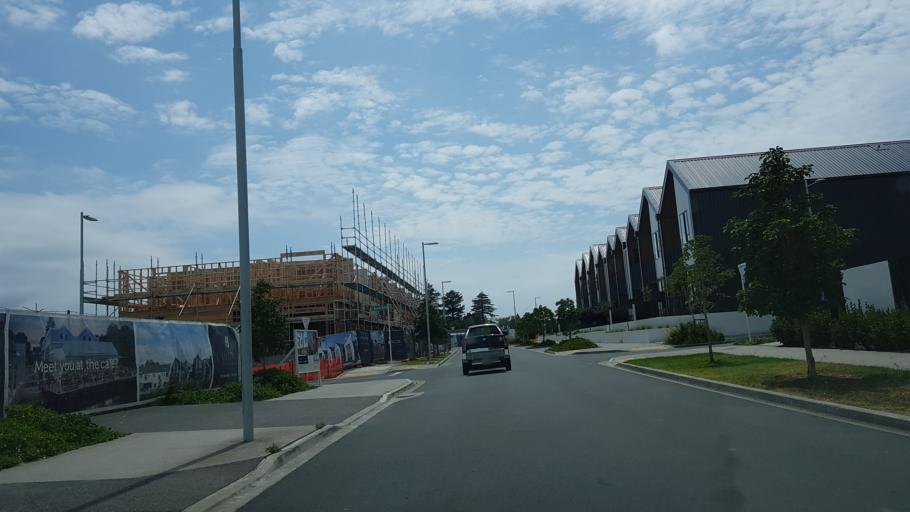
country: NZ
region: Auckland
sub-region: Auckland
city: Rosebank
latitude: -36.7893
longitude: 174.6617
